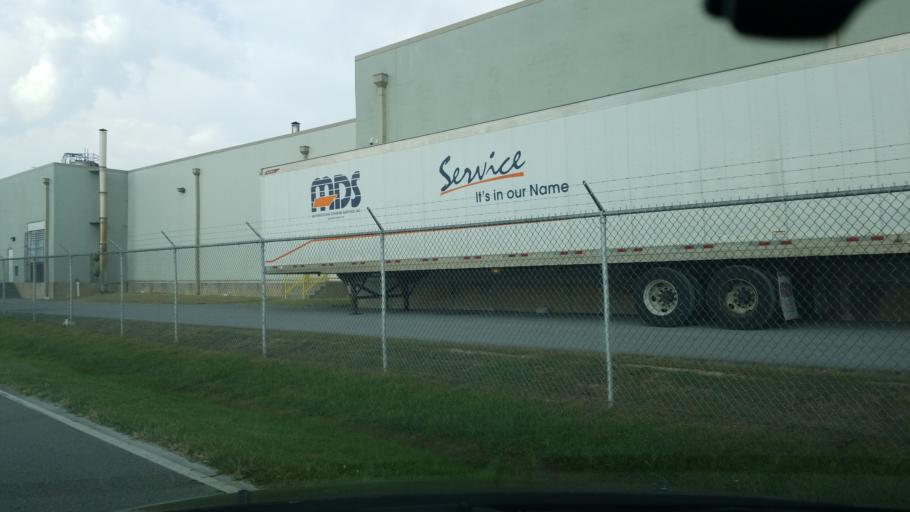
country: US
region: Tennessee
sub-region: Cumberland County
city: Crossville
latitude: 35.9596
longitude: -85.0365
